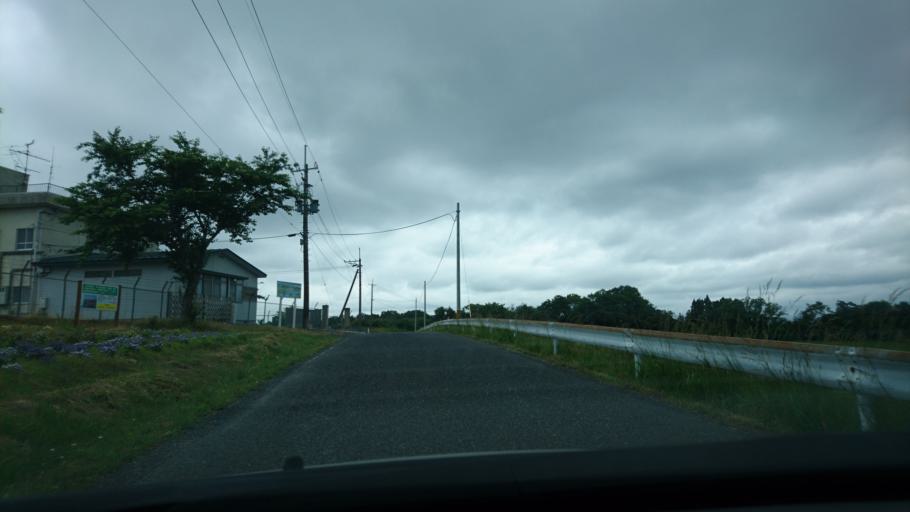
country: JP
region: Iwate
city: Ichinoseki
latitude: 38.8797
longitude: 141.2011
